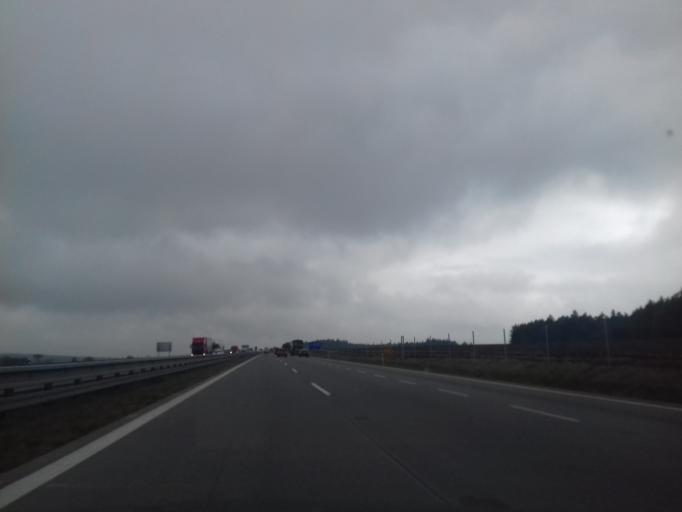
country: CZ
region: Vysocina
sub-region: Okres Pelhrimov
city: Zeliv
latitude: 49.6062
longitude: 15.1698
